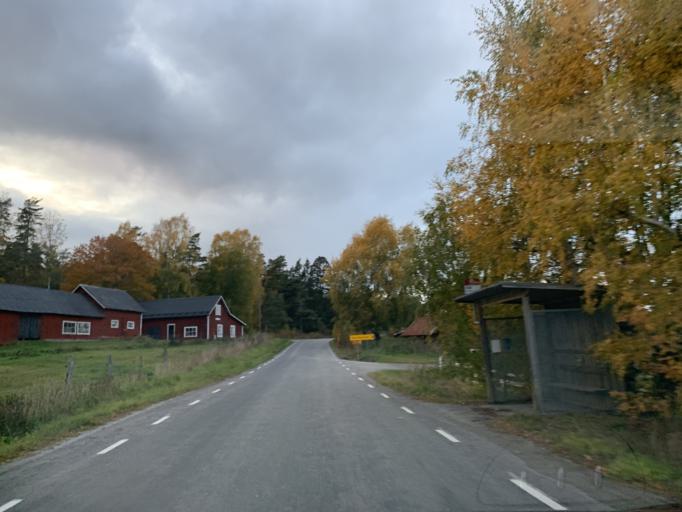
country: SE
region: Stockholm
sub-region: Nynashamns Kommun
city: Osmo
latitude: 58.9143
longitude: 17.7823
